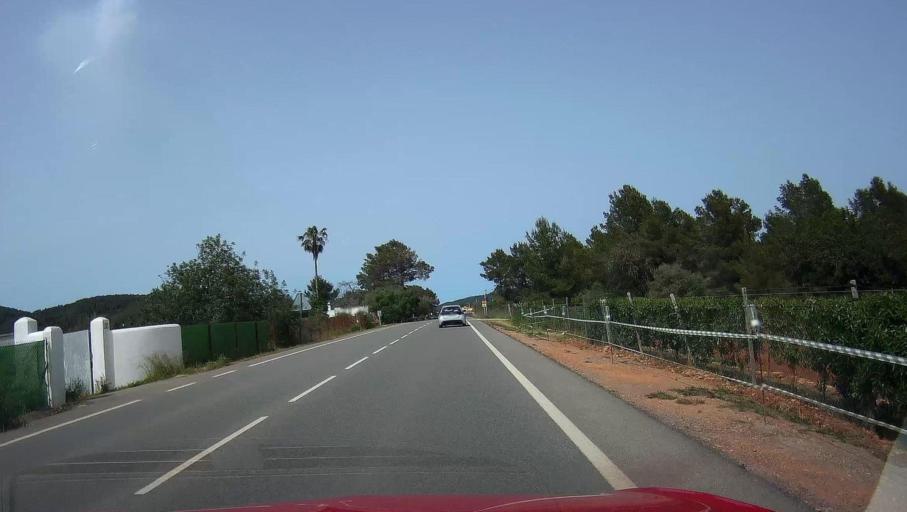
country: ES
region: Balearic Islands
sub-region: Illes Balears
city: Sant Joan de Labritja
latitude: 39.0286
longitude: 1.4882
